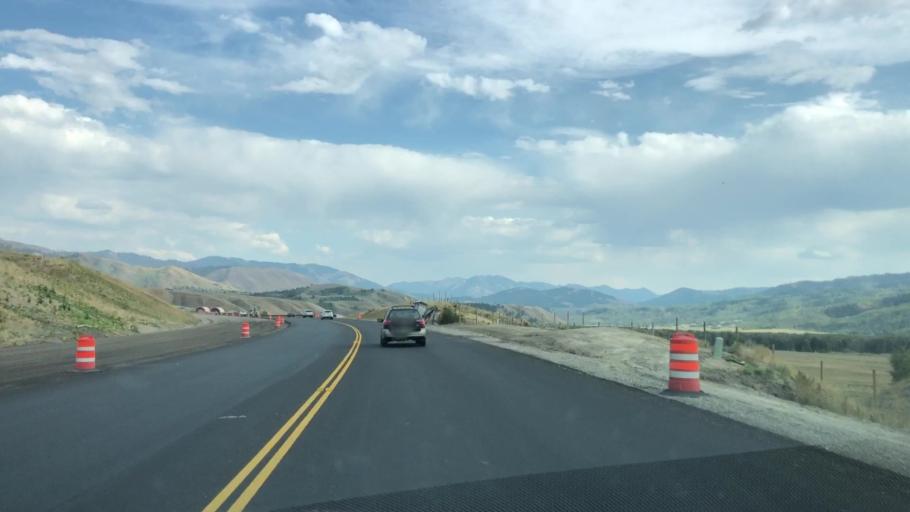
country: US
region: Wyoming
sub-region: Teton County
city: South Park
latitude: 43.4106
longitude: -110.7702
